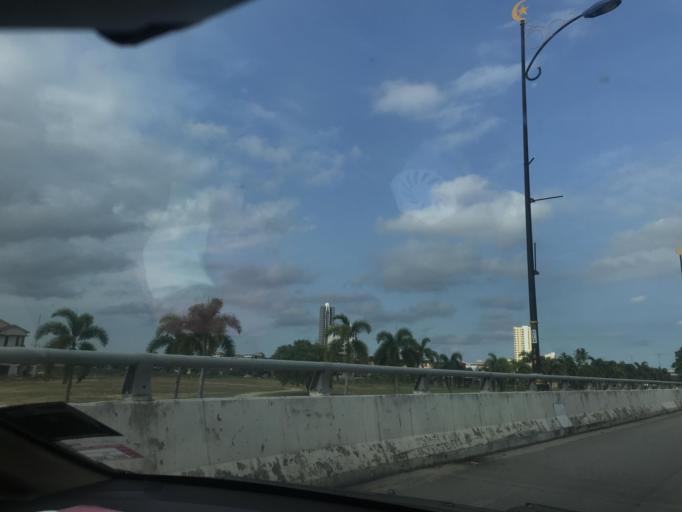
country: MY
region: Kelantan
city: Kota Bharu
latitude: 6.1160
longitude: 102.2320
